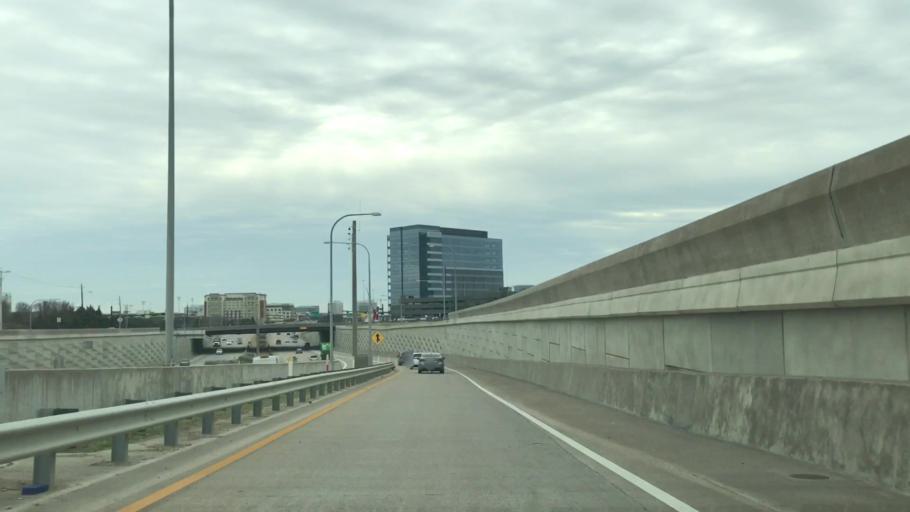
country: US
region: Texas
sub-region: Collin County
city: Frisco
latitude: 33.1097
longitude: -96.8238
